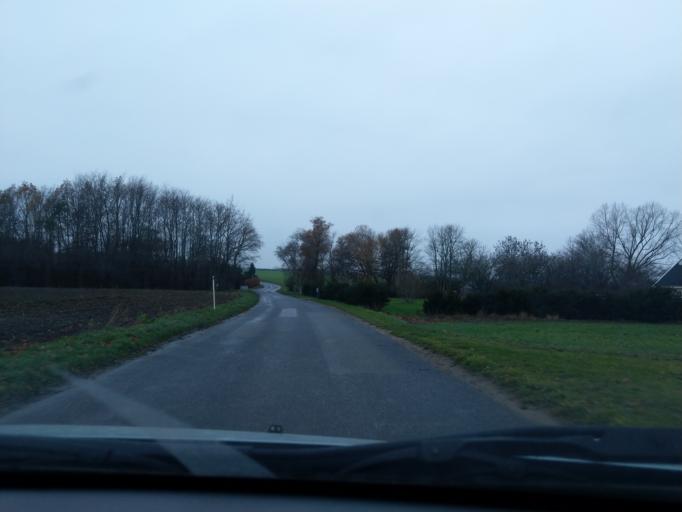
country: DK
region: Zealand
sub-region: Vordingborg Kommune
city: Praesto
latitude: 55.1115
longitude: 12.1018
